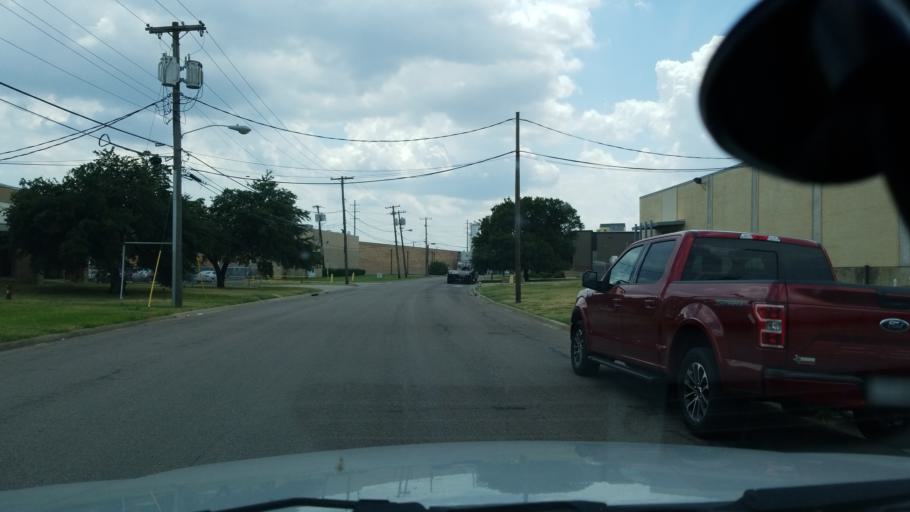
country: US
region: Texas
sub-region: Dallas County
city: Irving
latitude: 32.8322
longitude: -96.8841
